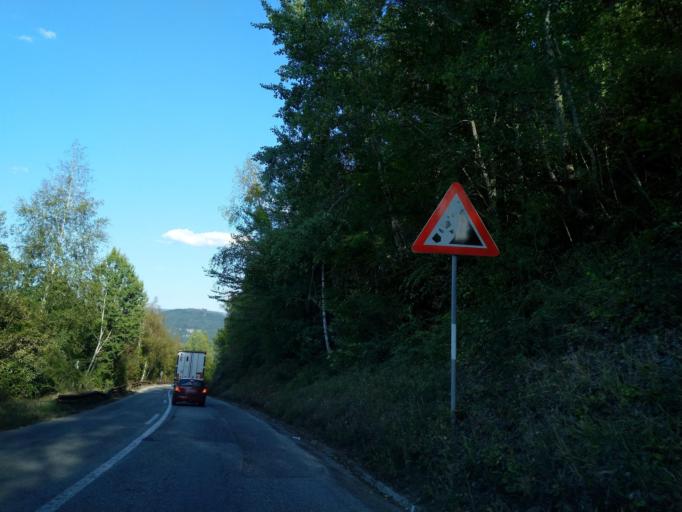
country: RS
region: Central Serbia
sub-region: Zlatiborski Okrug
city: Prijepolje
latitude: 43.3620
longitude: 19.5989
